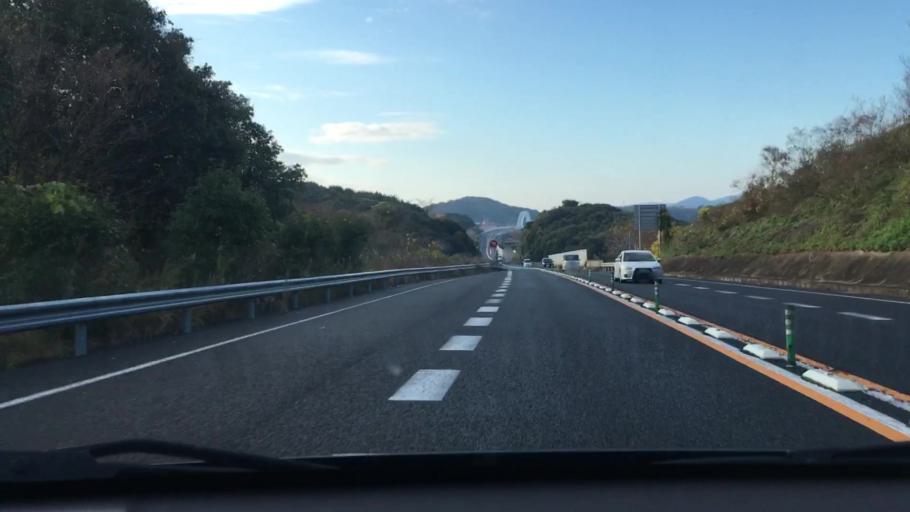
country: JP
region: Nagasaki
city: Sasebo
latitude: 33.0633
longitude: 129.7605
